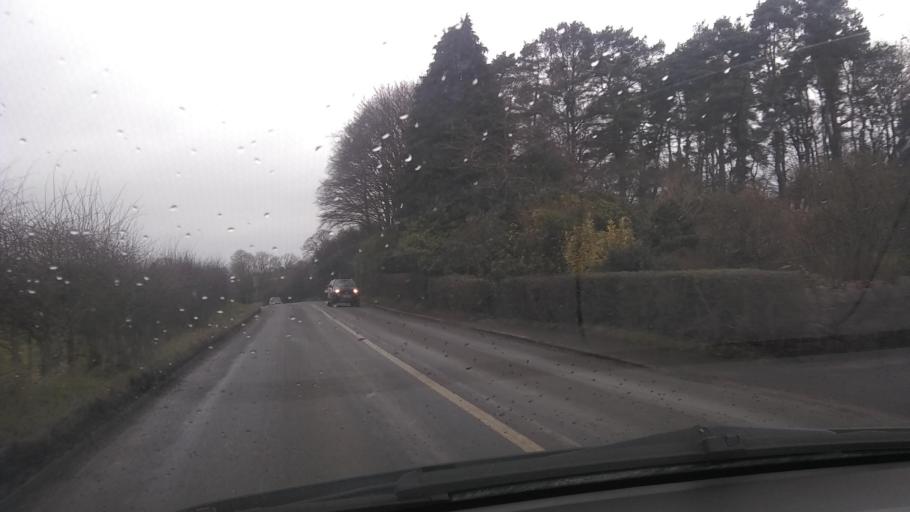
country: GB
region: England
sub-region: Worcestershire
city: Tenbury Wells
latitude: 52.3757
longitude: -2.6058
